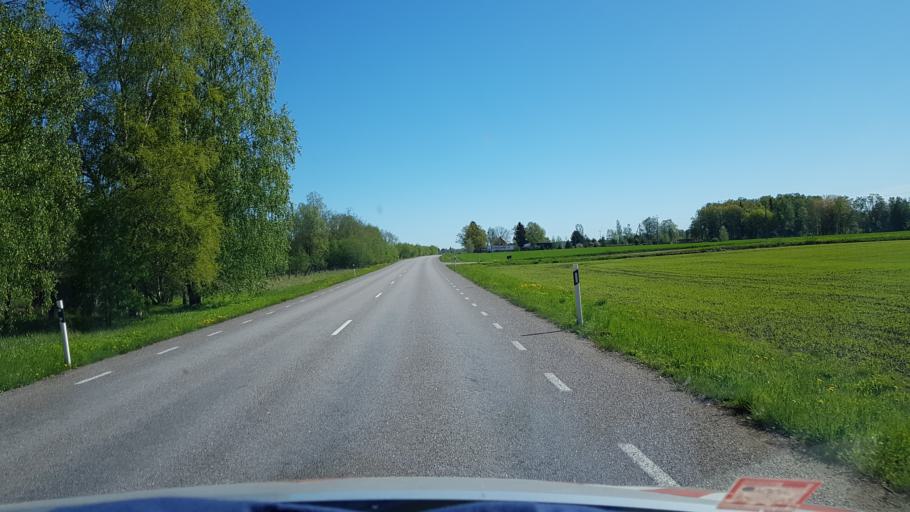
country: EE
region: Tartu
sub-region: Tartu linn
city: Tartu
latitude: 58.3921
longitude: 26.8149
